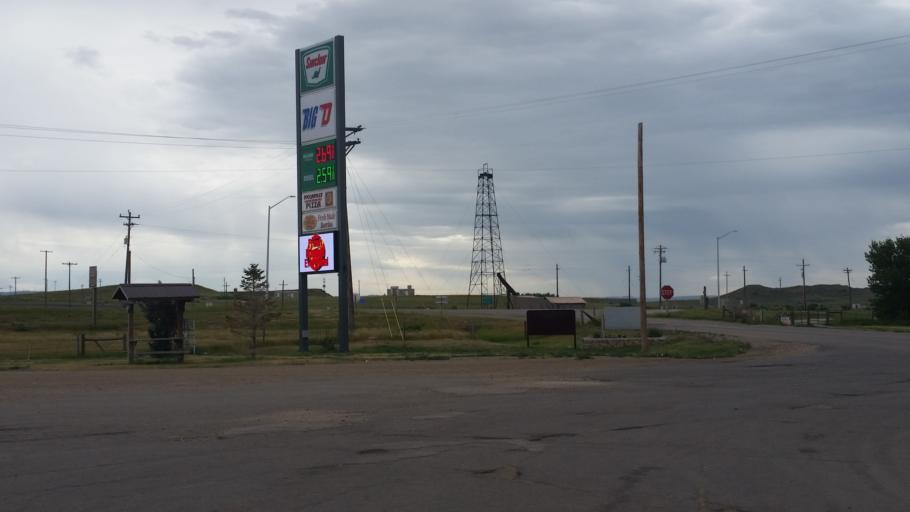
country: US
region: Wyoming
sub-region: Natrona County
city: Bar Nunn
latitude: 43.4101
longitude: -106.2713
